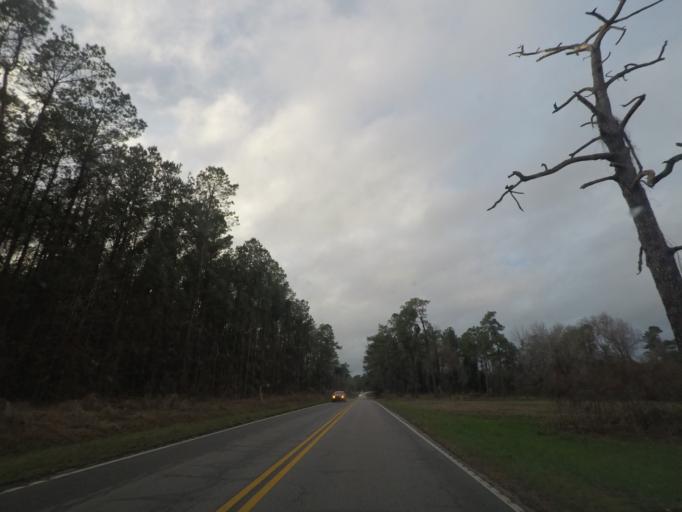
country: US
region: South Carolina
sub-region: Dorchester County
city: Saint George
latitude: 33.0572
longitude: -80.6214
